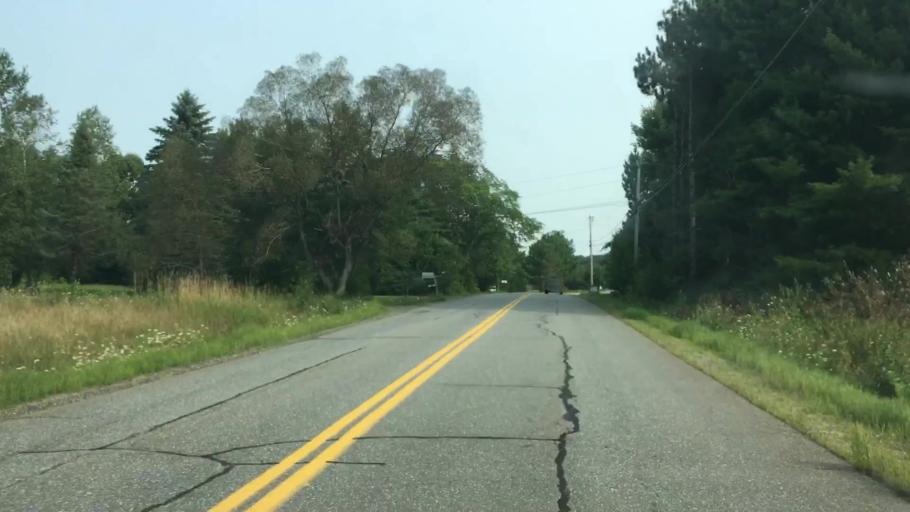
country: US
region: Maine
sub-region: Kennebec County
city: Chelsea
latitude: 44.3004
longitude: -69.6970
